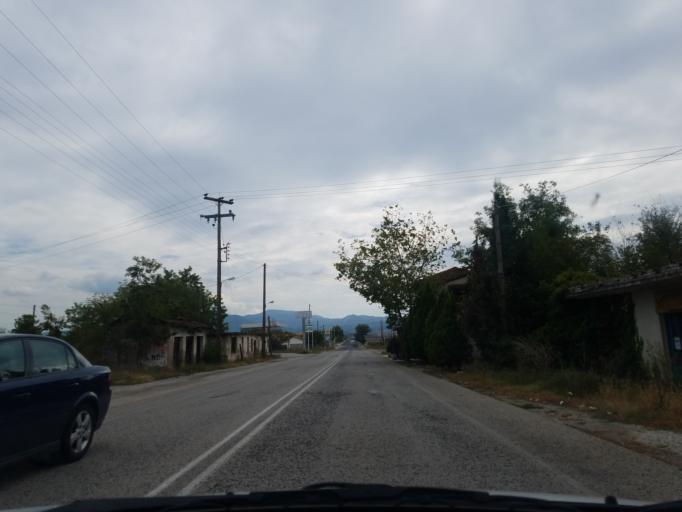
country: GR
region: Central Greece
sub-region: Nomos Fthiotidos
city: Omvriaki
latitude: 39.0772
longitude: 22.3154
